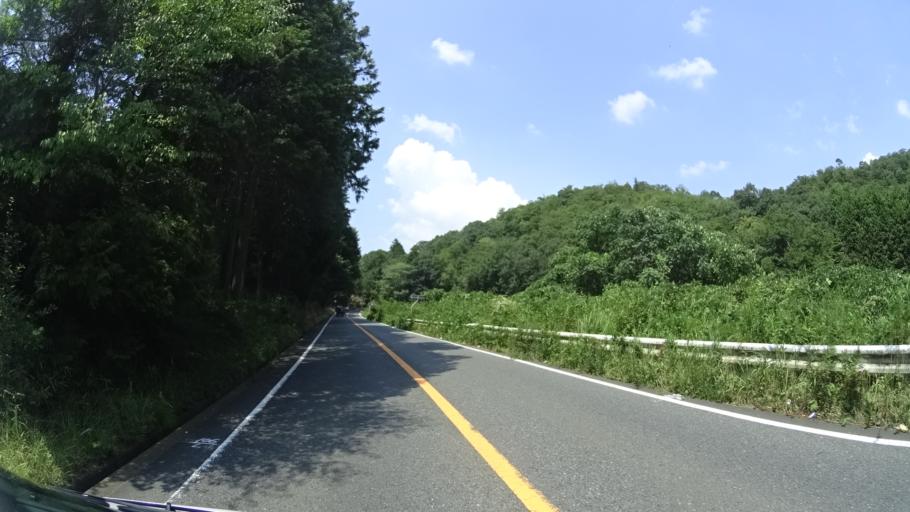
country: JP
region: Kyoto
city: Fukuchiyama
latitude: 35.2618
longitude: 135.1467
